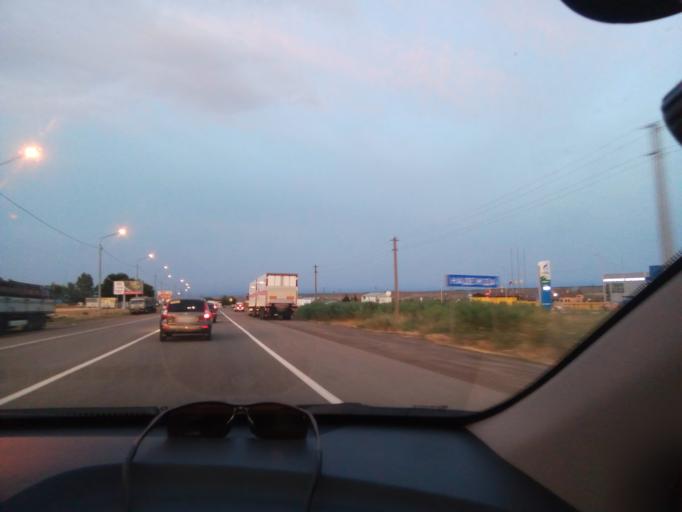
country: RU
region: Stavropol'skiy
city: Mikhaylovsk
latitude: 45.0575
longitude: 42.0935
